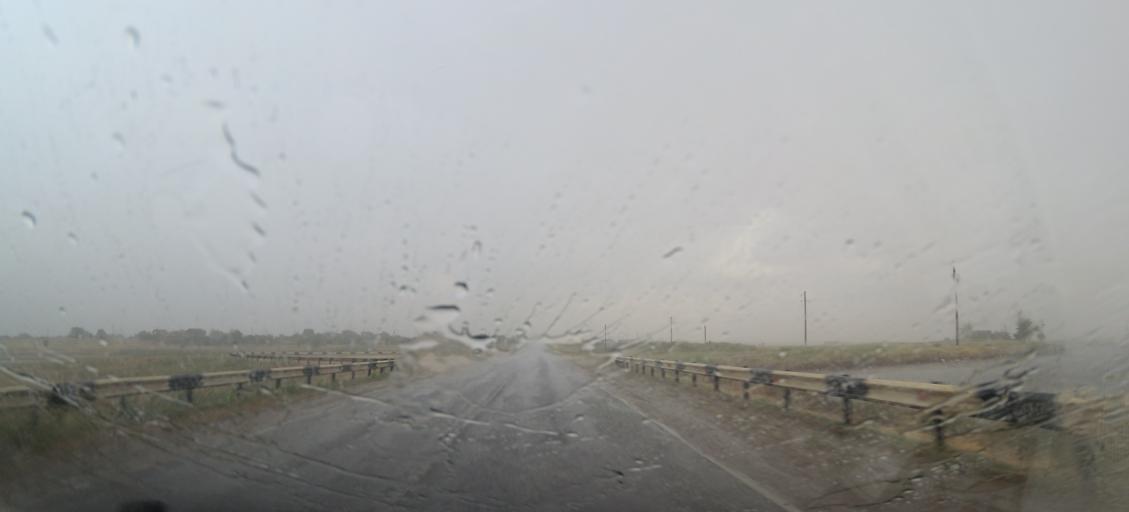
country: RU
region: Rostov
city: Proletarsk
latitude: 46.6793
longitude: 41.7093
